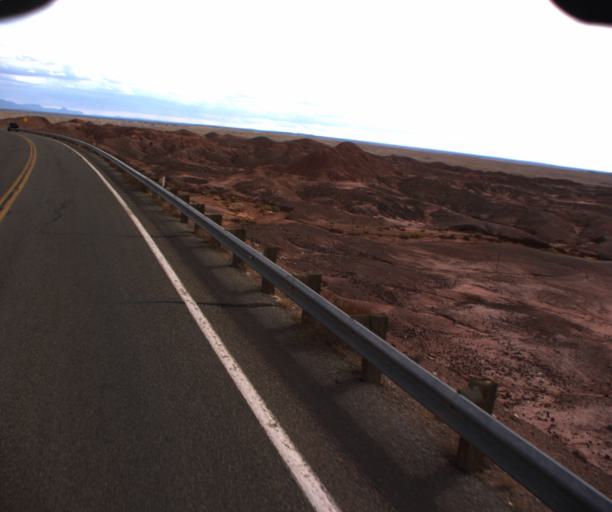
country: US
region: Arizona
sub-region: Apache County
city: Many Farms
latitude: 36.4688
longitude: -109.5552
